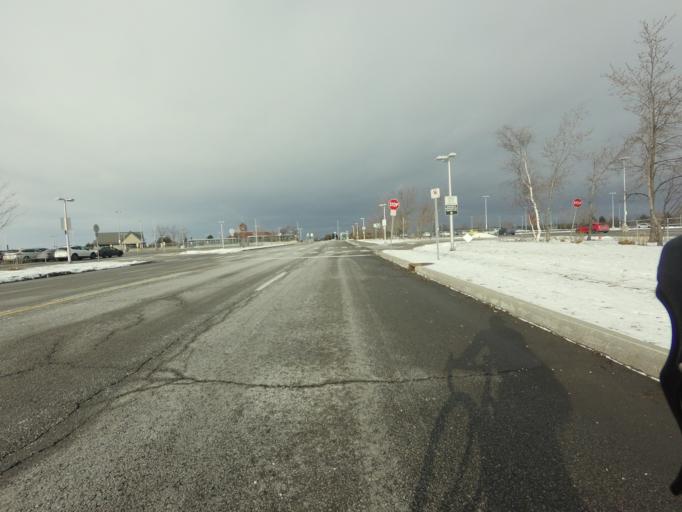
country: CA
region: Ontario
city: Bells Corners
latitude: 45.2979
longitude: -75.7350
